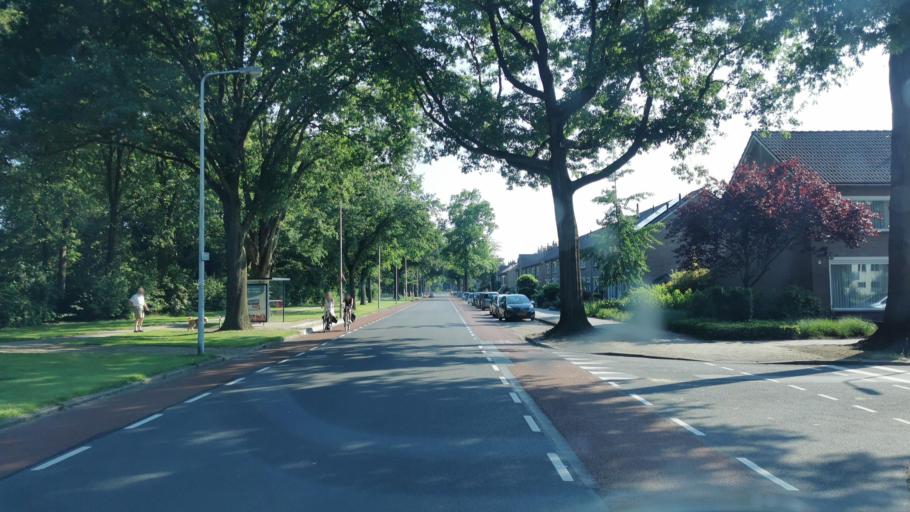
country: NL
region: Overijssel
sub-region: Gemeente Oldenzaal
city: Oldenzaal
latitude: 52.3120
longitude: 6.9108
